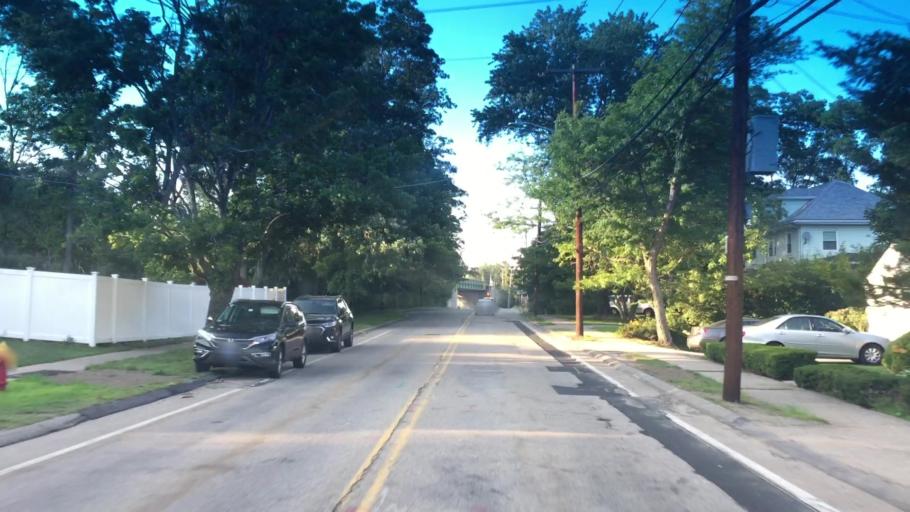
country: US
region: Massachusetts
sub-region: Norfolk County
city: Norwood
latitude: 42.2117
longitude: -71.1908
